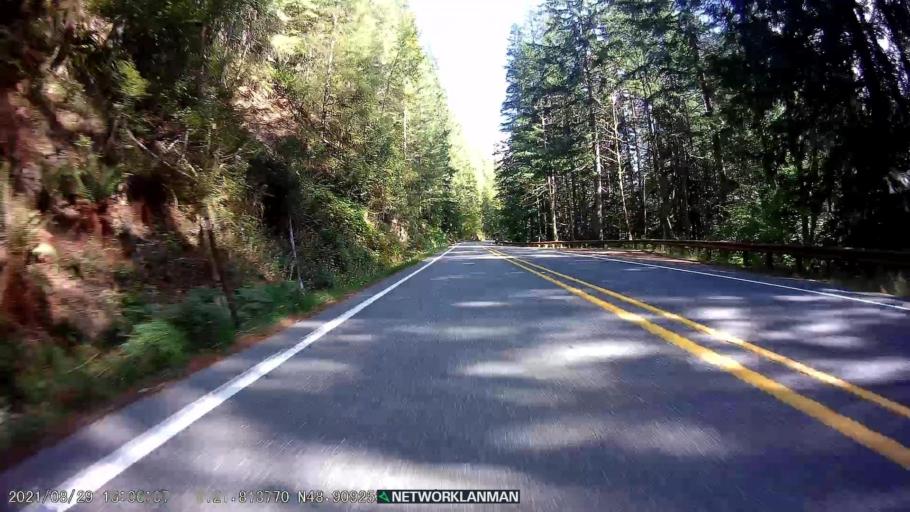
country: CA
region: British Columbia
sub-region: Fraser Valley Regional District
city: Chilliwack
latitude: 48.9095
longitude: -121.8143
